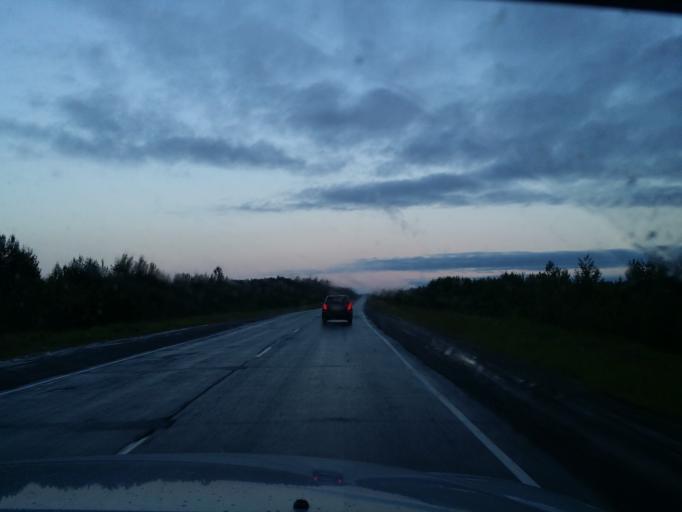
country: RU
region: Khanty-Mansiyskiy Avtonomnyy Okrug
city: Salym
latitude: 60.2255
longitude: 71.8691
